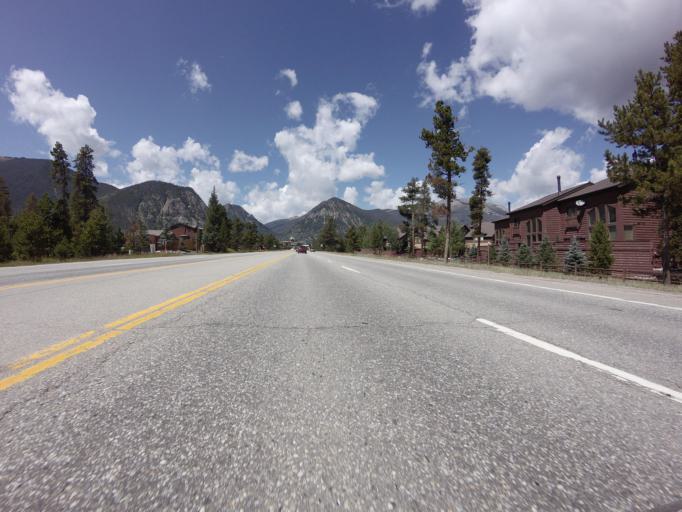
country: US
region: Colorado
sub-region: Summit County
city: Frisco
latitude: 39.5738
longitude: -106.0865
